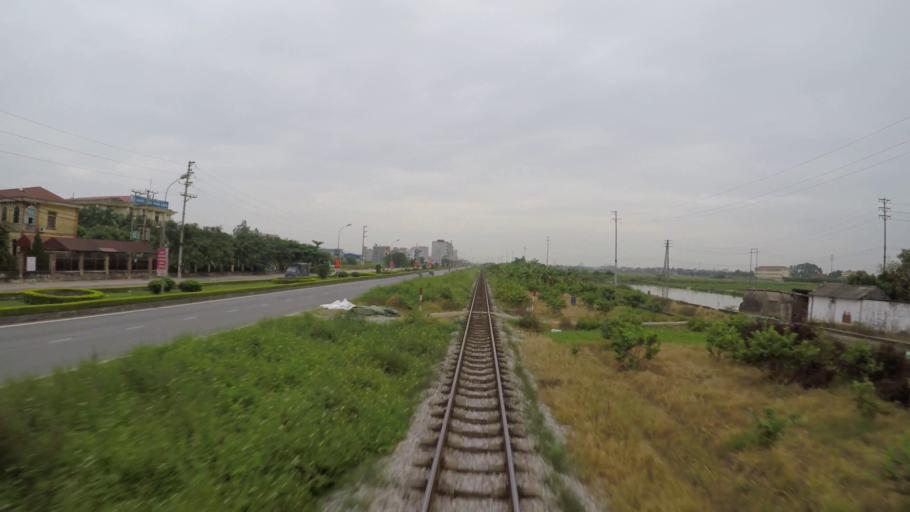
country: VN
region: Hung Yen
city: Nhu Quynh
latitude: 20.9816
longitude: 106.0256
